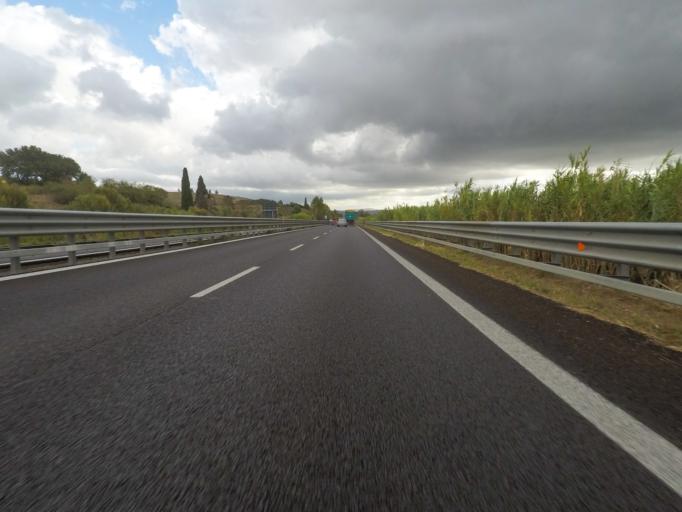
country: IT
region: Tuscany
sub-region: Provincia di Siena
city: Arbia
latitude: 43.3061
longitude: 11.4368
